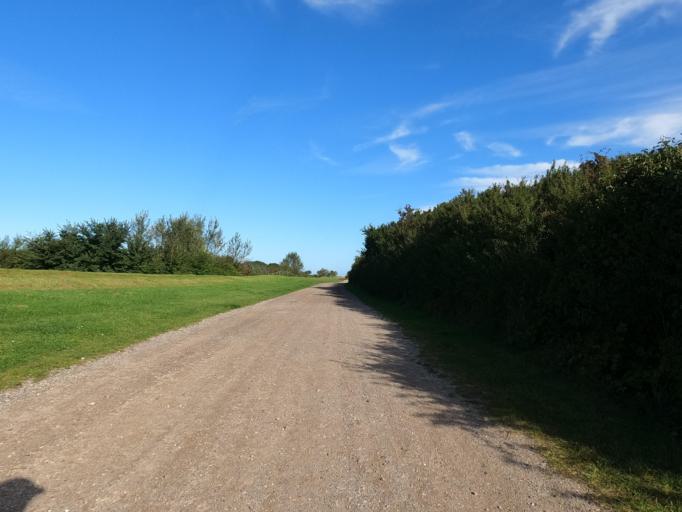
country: DE
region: Schleswig-Holstein
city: Dahme
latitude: 54.2766
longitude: 11.0830
